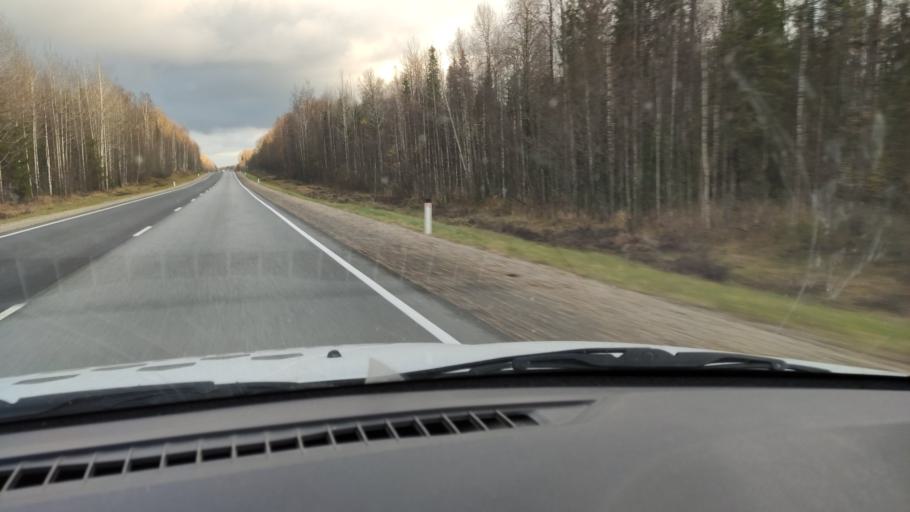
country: RU
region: Kirov
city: Chernaya Kholunitsa
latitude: 58.7890
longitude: 51.8926
